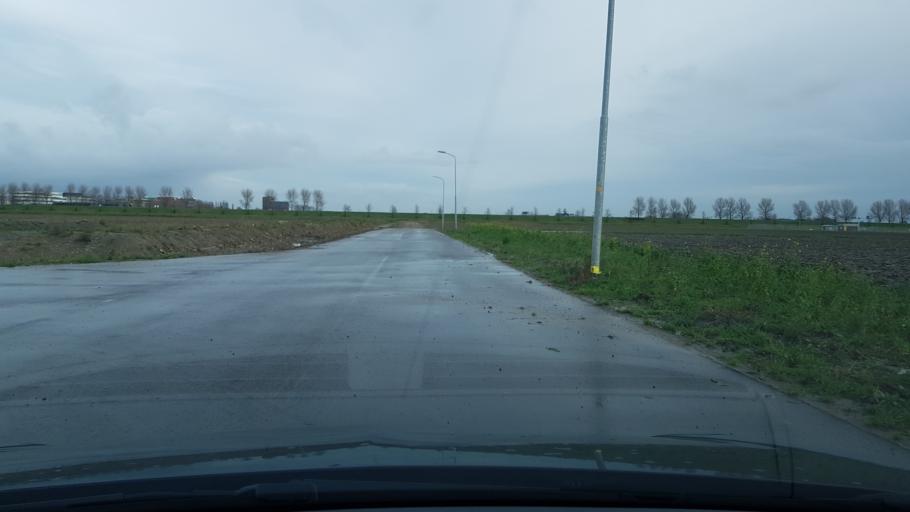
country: NL
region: North Holland
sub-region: Gemeente Haarlemmermeer
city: Hoofddorp
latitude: 52.2810
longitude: 4.7042
